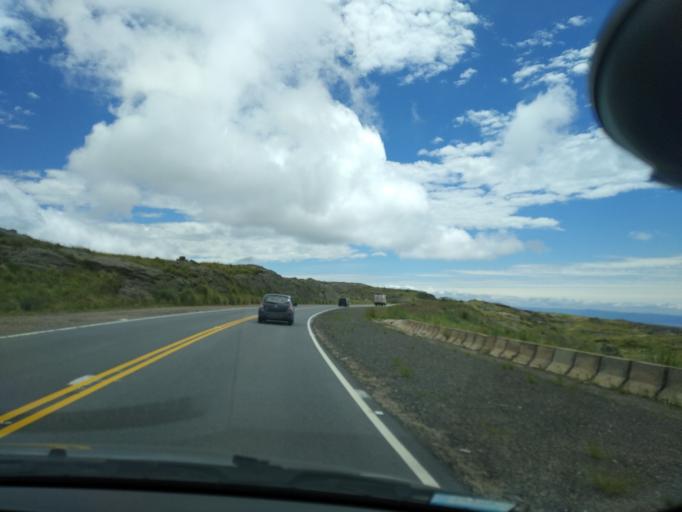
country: AR
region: Cordoba
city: Cuesta Blanca
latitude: -31.6032
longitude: -64.7206
